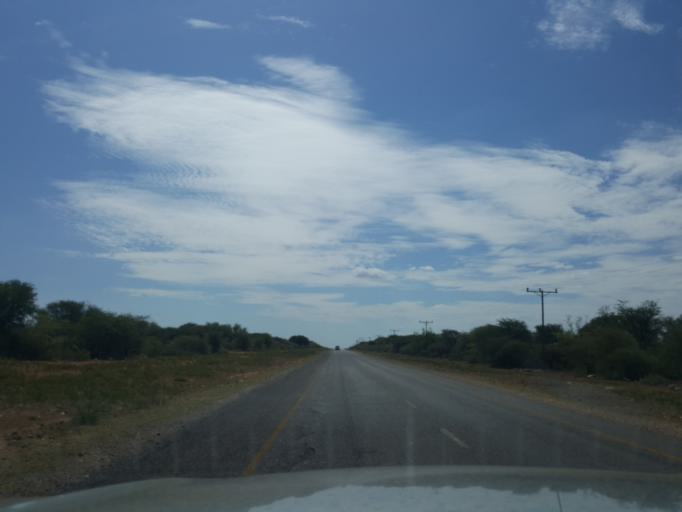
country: BW
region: Kweneng
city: Letlhakeng
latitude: -24.1490
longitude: 25.1541
